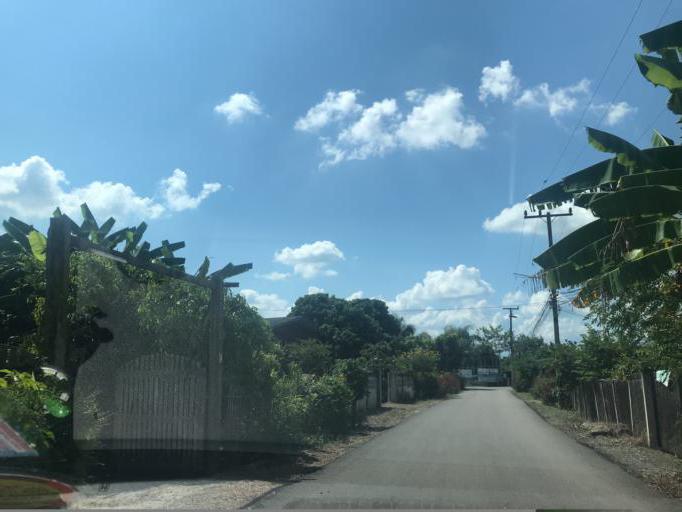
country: TH
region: Chiang Mai
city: Mae Wang
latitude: 18.5635
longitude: 98.8397
